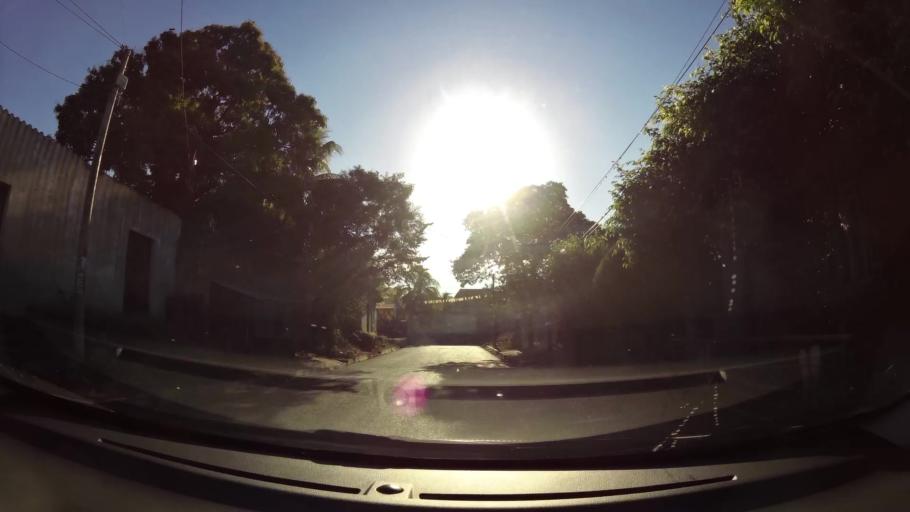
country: SV
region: Sonsonate
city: Sonsonate
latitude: 13.7063
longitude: -89.7155
